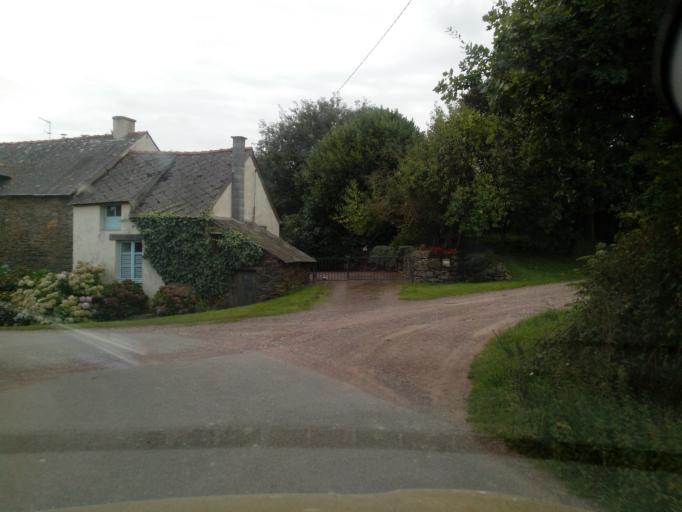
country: FR
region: Brittany
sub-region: Departement du Morbihan
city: Mauron
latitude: 48.0672
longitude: -2.3095
